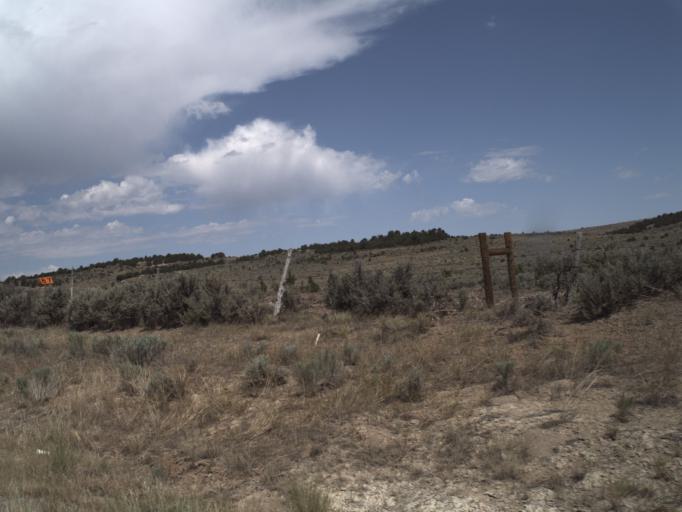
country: US
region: Utah
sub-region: Utah County
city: Genola
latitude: 39.9444
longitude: -112.2116
